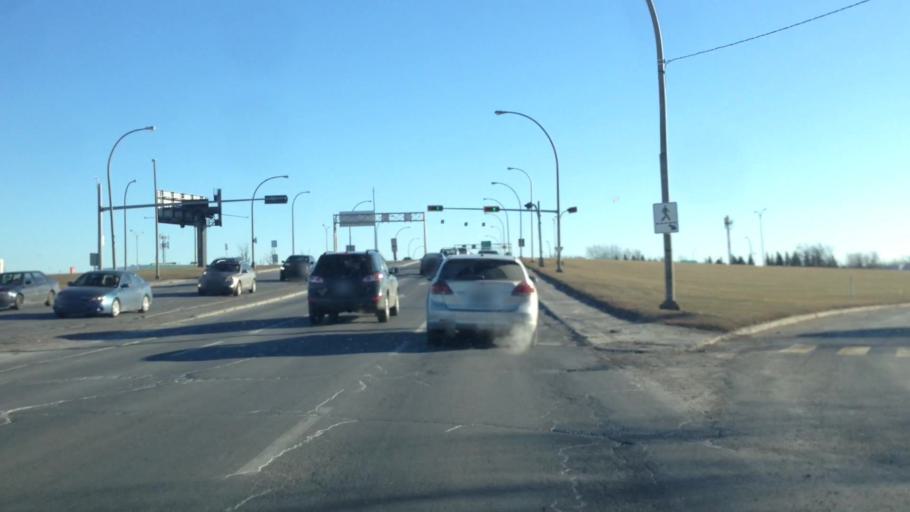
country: CA
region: Quebec
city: Dollard-Des Ormeaux
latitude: 45.4817
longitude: -73.7947
